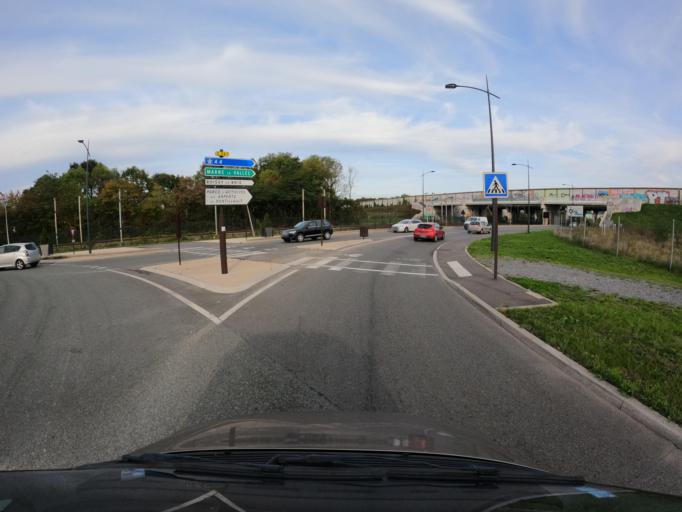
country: FR
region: Ile-de-France
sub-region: Departement de Seine-et-Marne
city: Emerainville
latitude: 48.8034
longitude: 2.6252
